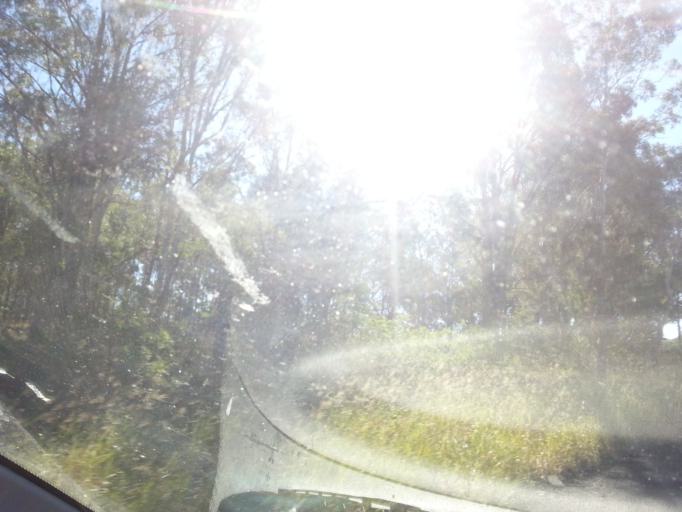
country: AU
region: New South Wales
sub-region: Wollongong
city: Dapto
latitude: -34.5187
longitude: 150.7812
